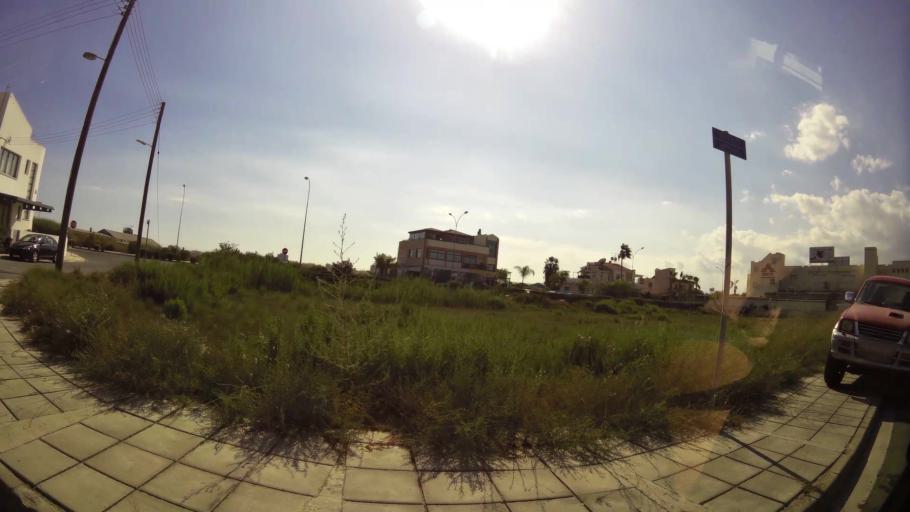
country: CY
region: Larnaka
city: Livadia
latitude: 34.9446
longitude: 33.6366
